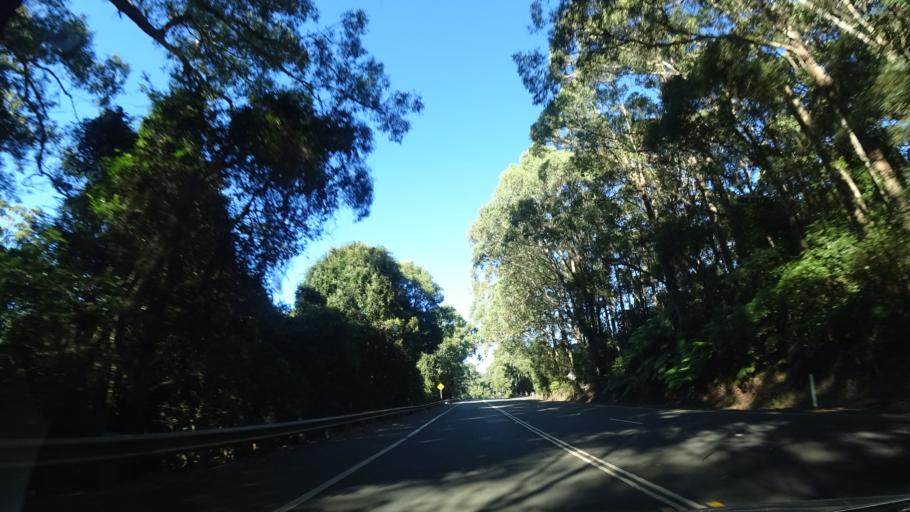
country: AU
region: New South Wales
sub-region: Blue Mountains Municipality
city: Blackheath
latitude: -33.5456
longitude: 150.4255
